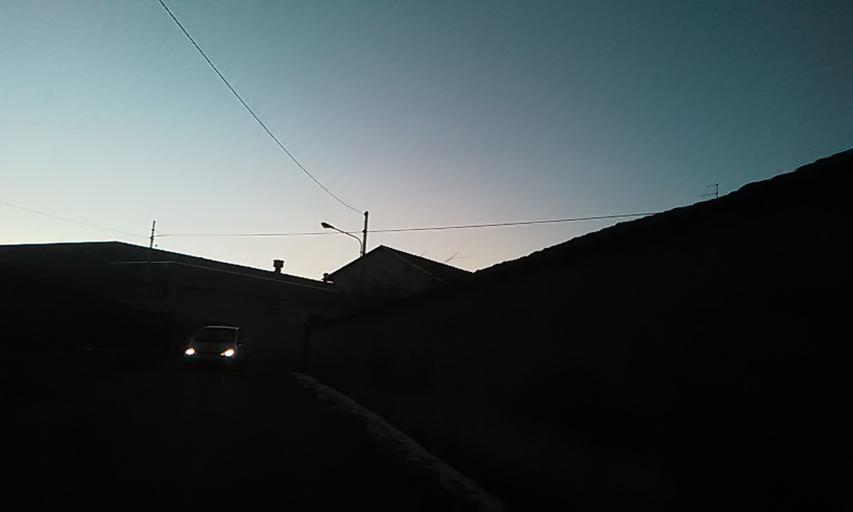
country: IT
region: Piedmont
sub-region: Provincia di Biella
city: Biella
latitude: 45.5587
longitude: 8.0442
